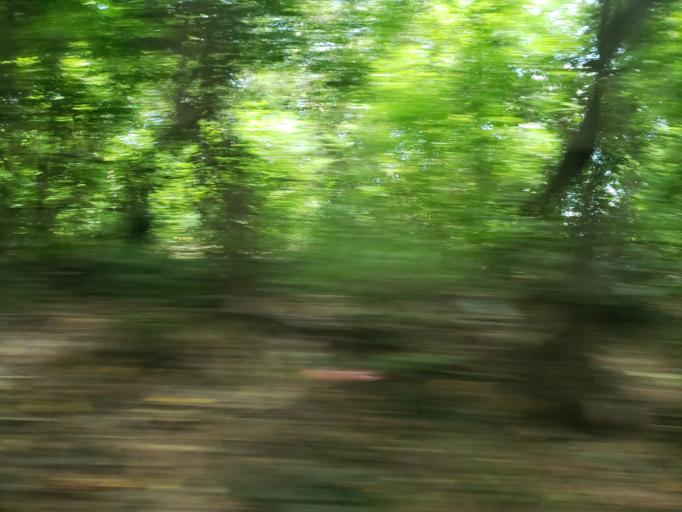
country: ID
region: Bali
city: Kangin
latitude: -8.8254
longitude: 115.1498
